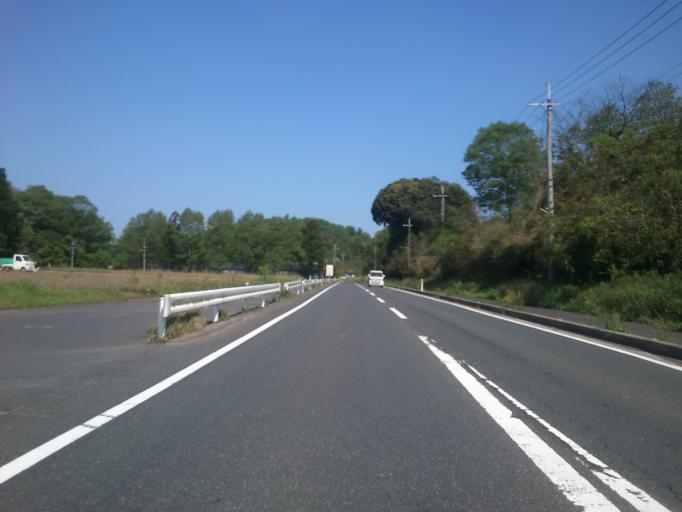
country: JP
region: Kyoto
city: Miyazu
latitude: 35.6785
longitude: 135.0701
